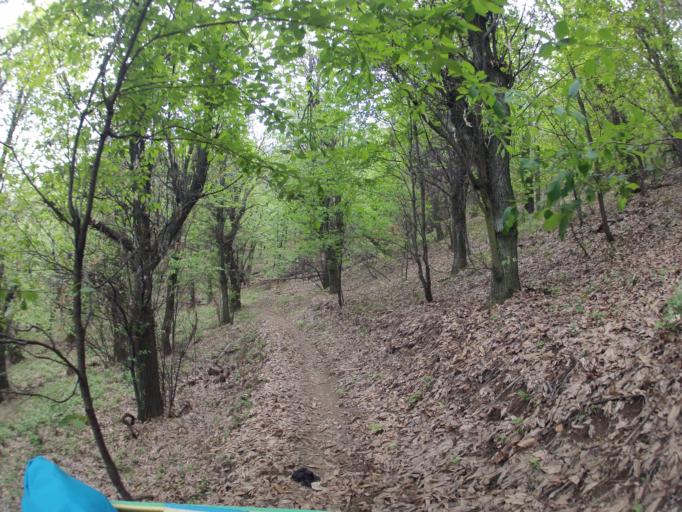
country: IT
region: Piedmont
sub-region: Provincia di Cuneo
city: Peveragno
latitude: 44.3281
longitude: 7.5938
